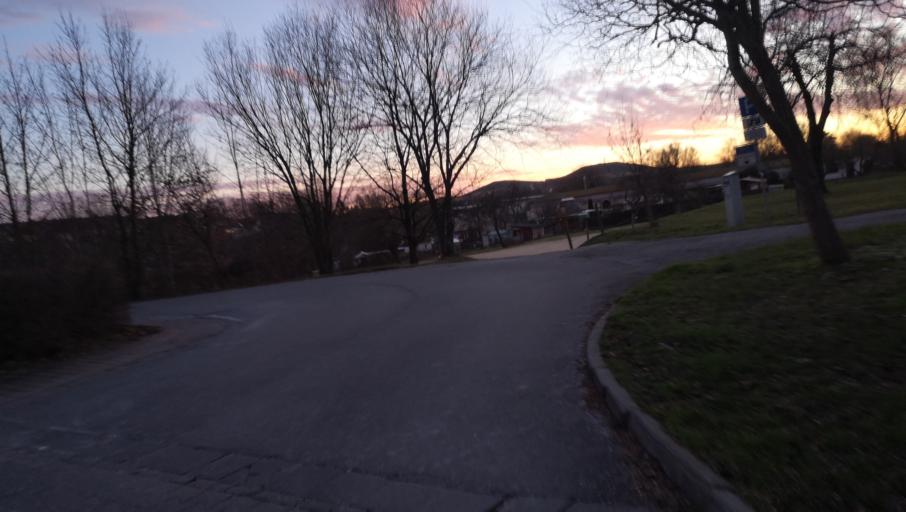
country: DE
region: Thuringia
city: Ronneburg
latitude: 50.8661
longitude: 12.1766
